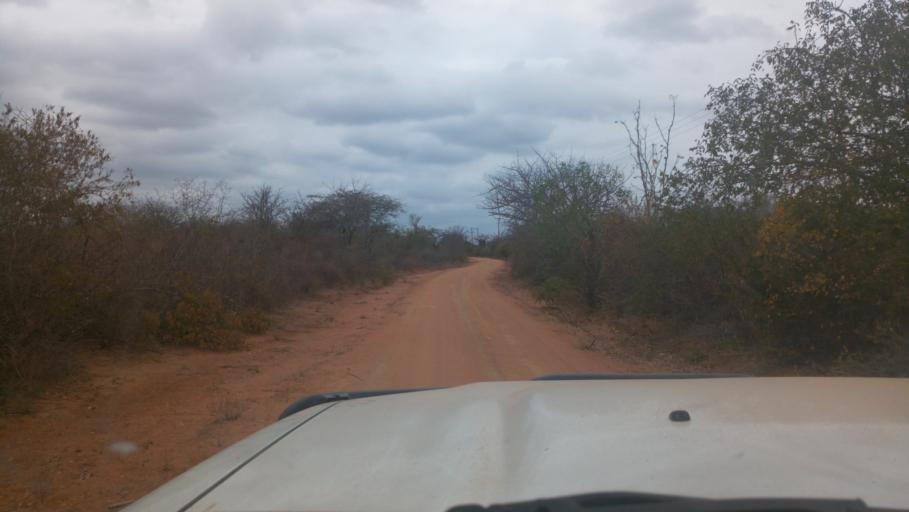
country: KE
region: Makueni
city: Wote
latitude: -1.8599
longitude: 37.9872
